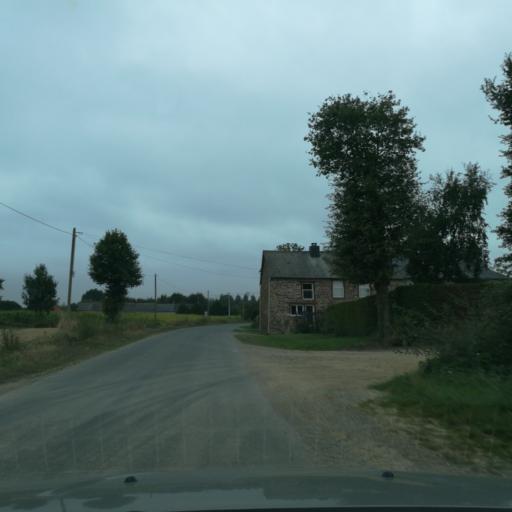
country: FR
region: Brittany
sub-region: Departement d'Ille-et-Vilaine
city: Montauban-de-Bretagne
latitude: 48.1863
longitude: -2.0186
